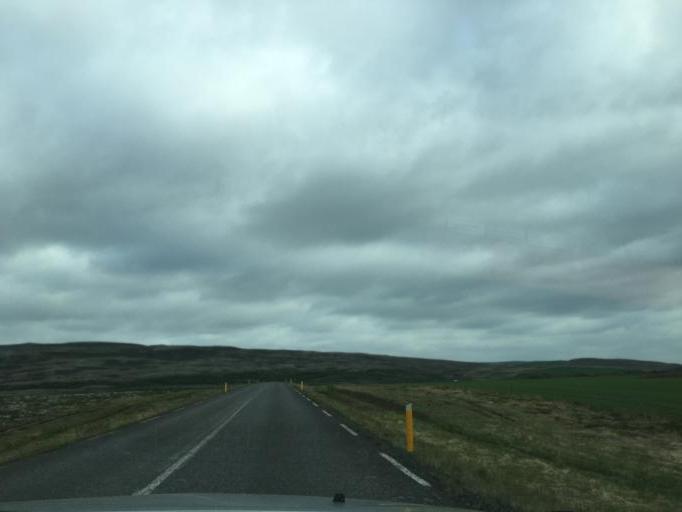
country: IS
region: South
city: Vestmannaeyjar
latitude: 64.2683
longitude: -20.2254
